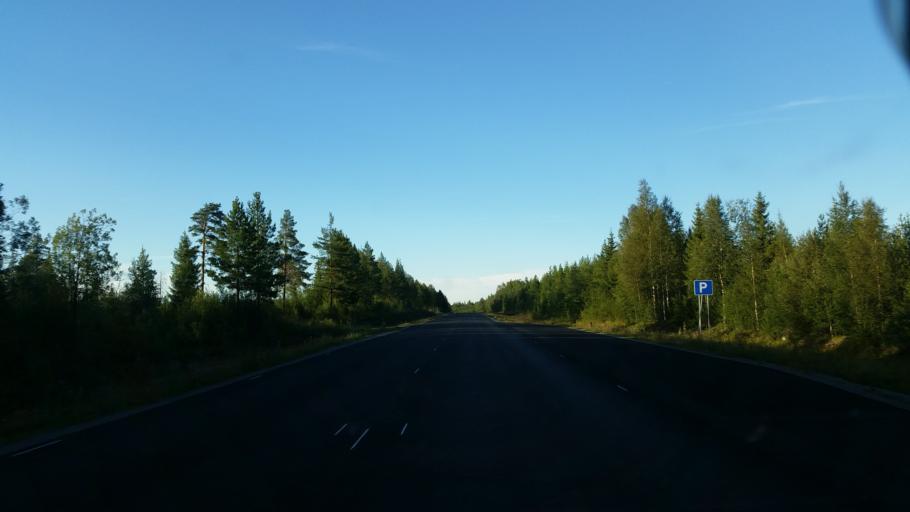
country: SE
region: Vaesterbotten
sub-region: Dorotea Kommun
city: Dorotea
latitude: 64.3299
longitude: 16.6319
